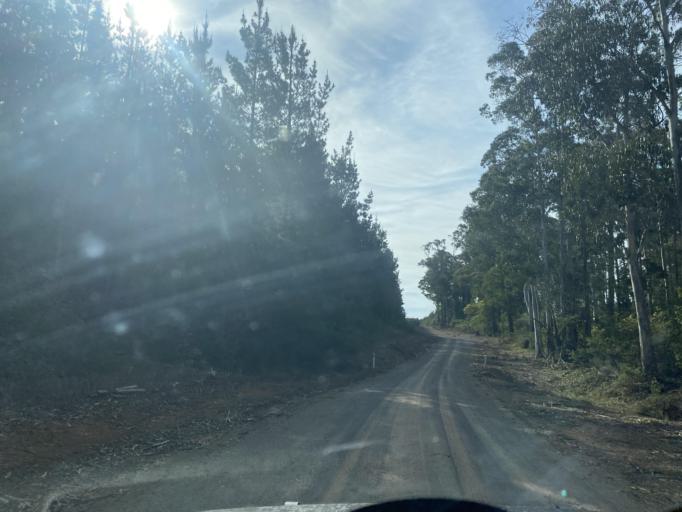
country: AU
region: Victoria
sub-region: Mansfield
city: Mansfield
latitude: -36.8799
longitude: 146.1888
